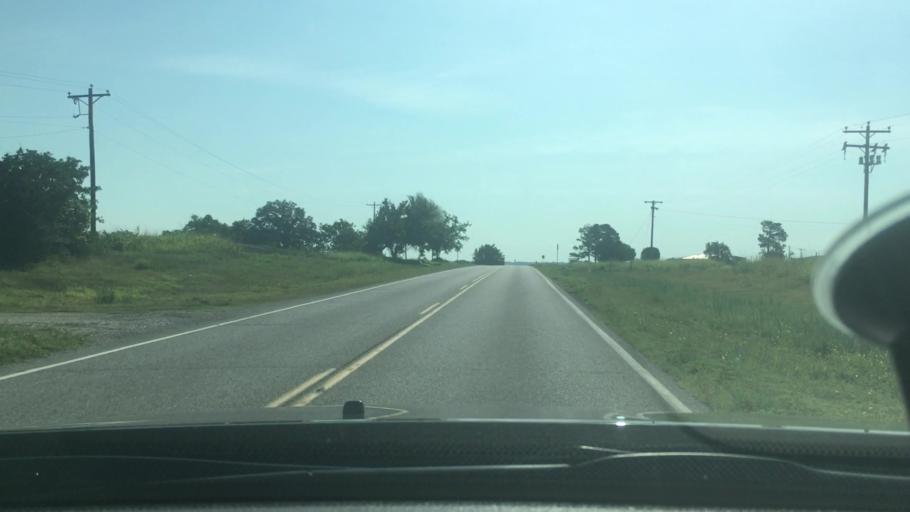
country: US
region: Oklahoma
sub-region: Garvin County
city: Wynnewood
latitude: 34.6517
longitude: -97.2285
